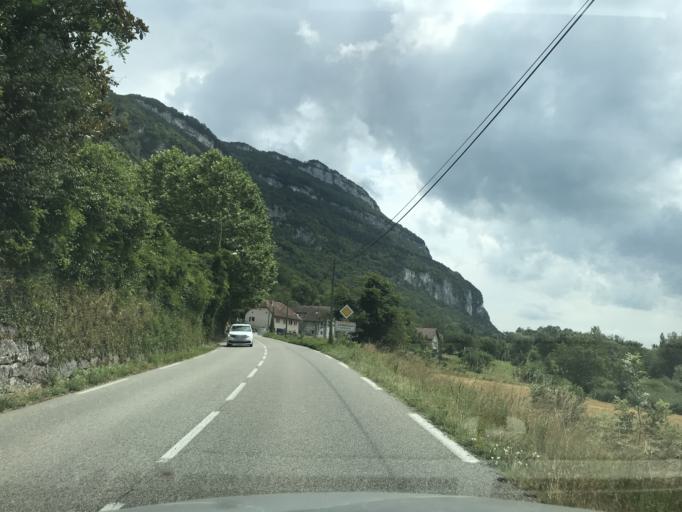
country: FR
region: Rhone-Alpes
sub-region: Departement de la Savoie
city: Chatillon
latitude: 45.8032
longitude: 5.8557
